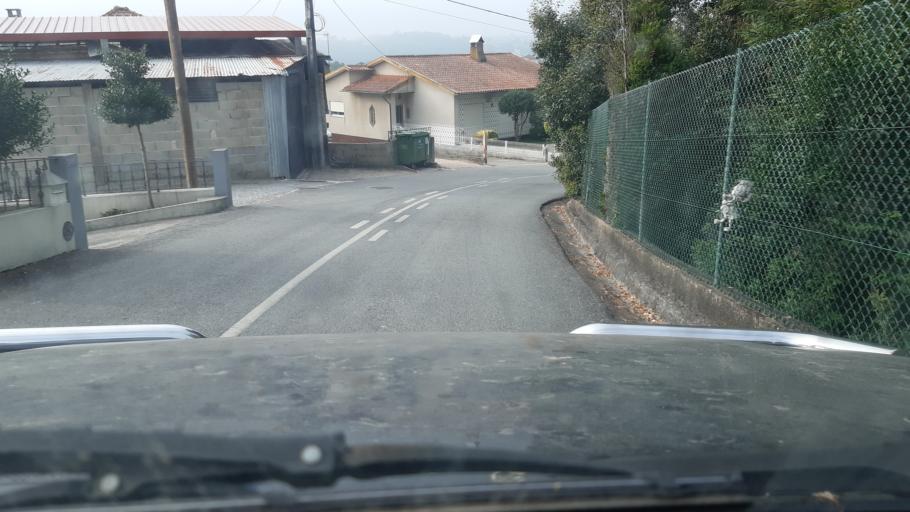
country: PT
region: Aveiro
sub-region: Agueda
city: Agueda
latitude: 40.5809
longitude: -8.4547
